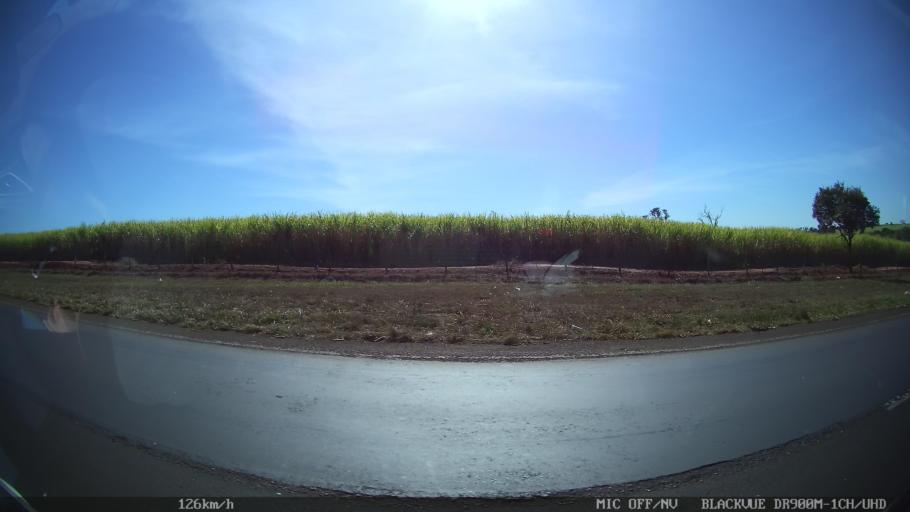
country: BR
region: Sao Paulo
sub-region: Barretos
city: Barretos
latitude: -20.5616
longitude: -48.6540
